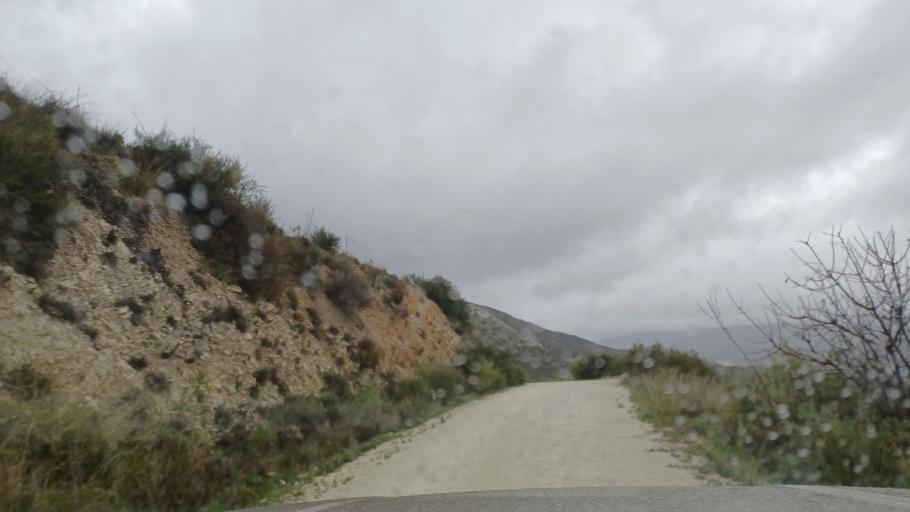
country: CY
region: Limassol
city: Pachna
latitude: 34.7953
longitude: 32.6944
